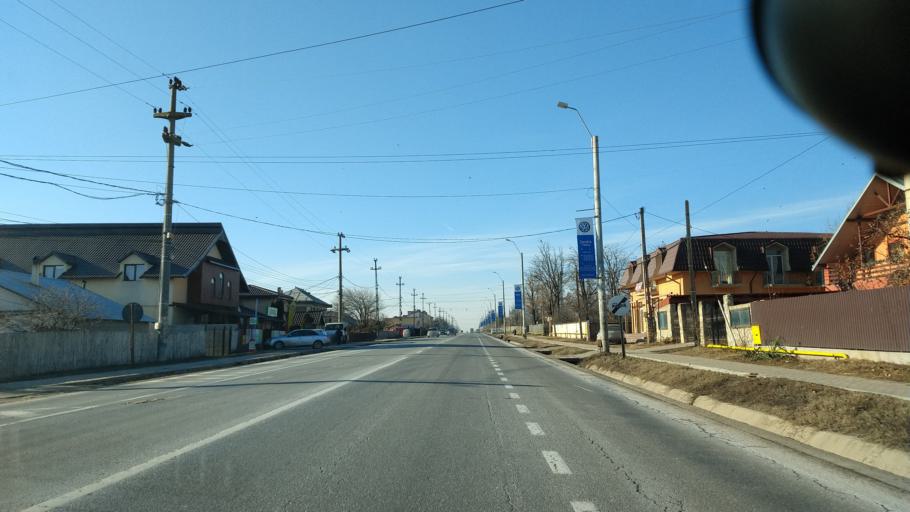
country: RO
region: Iasi
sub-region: Comuna Letcani
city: Letcani
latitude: 47.1953
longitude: 27.4125
